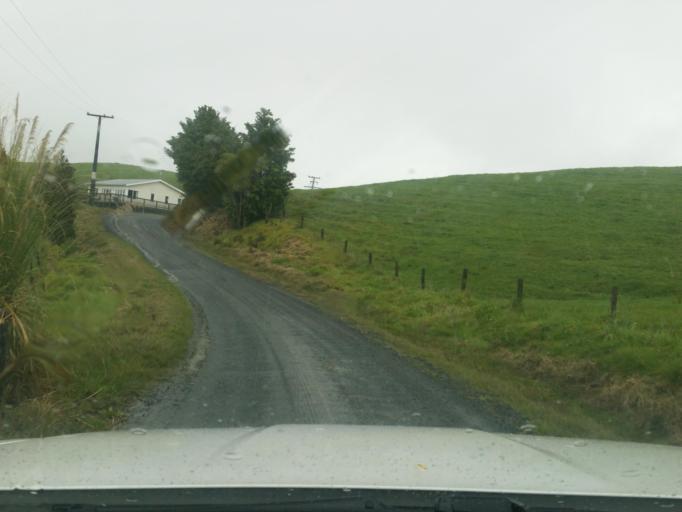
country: NZ
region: Northland
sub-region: Kaipara District
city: Dargaville
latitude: -35.8784
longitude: 174.0000
